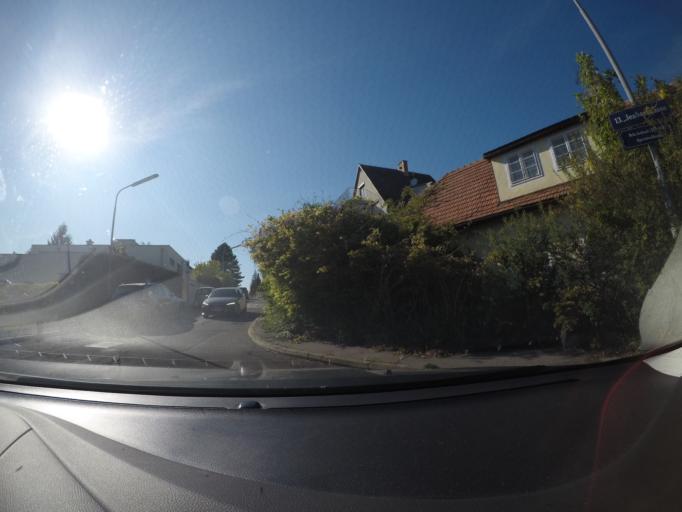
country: AT
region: Lower Austria
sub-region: Politischer Bezirk Modling
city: Perchtoldsdorf
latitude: 48.1675
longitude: 16.2639
